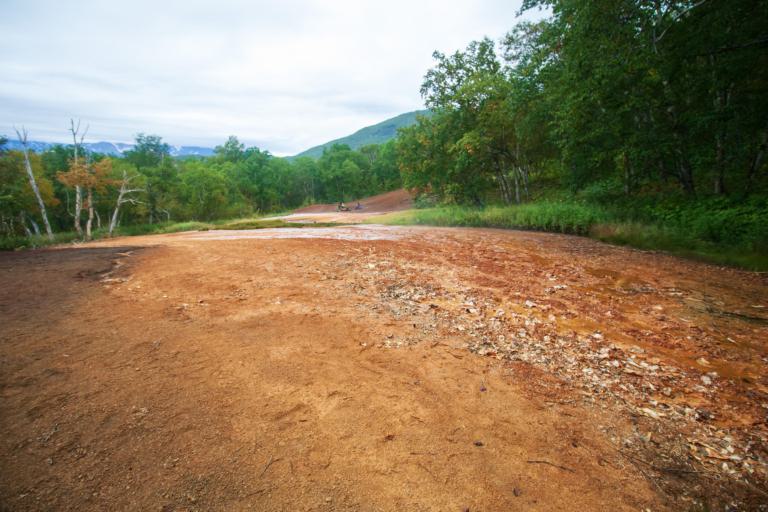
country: RU
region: Kamtsjatka
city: Petropavlovsk-Kamchatsky
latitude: 53.5548
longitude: 158.8209
